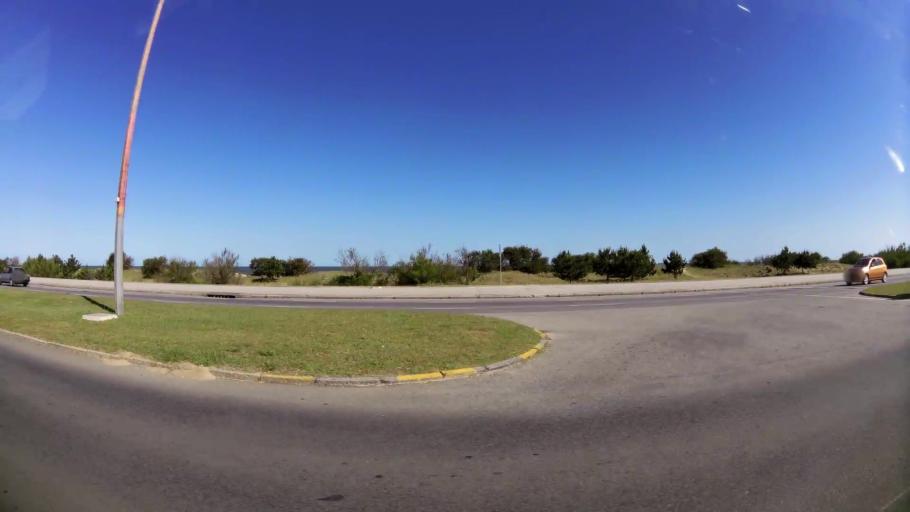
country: UY
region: Canelones
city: Barra de Carrasco
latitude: -34.8831
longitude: -56.0375
